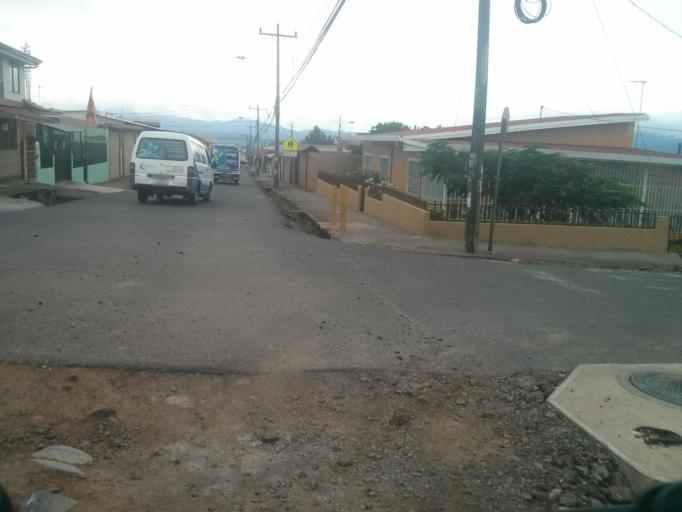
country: CR
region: Heredia
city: Angeles
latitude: 10.0178
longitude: -84.0573
